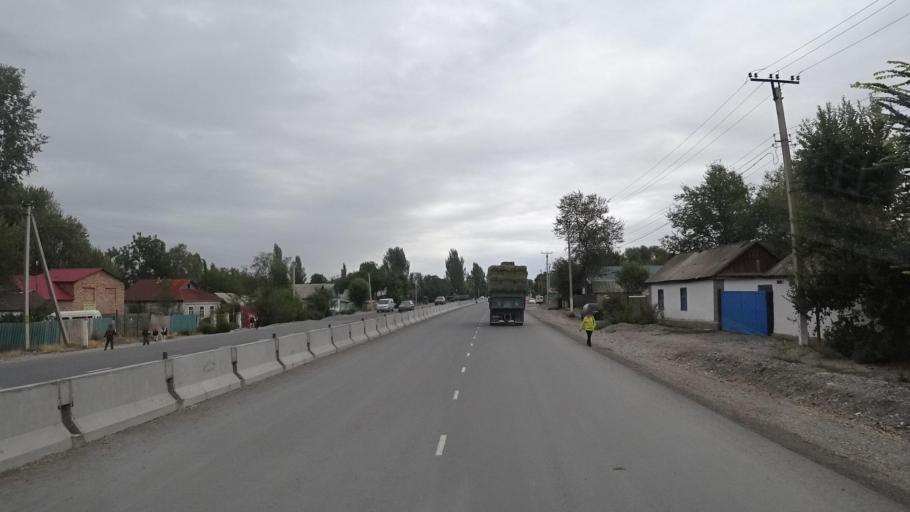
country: KG
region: Chuy
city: Kara-Balta
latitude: 42.8291
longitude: 73.8844
